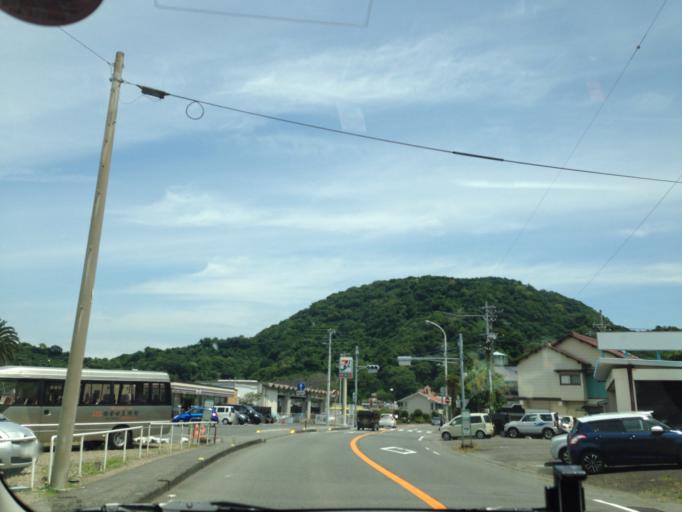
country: JP
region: Shizuoka
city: Numazu
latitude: 35.0213
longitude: 138.8976
